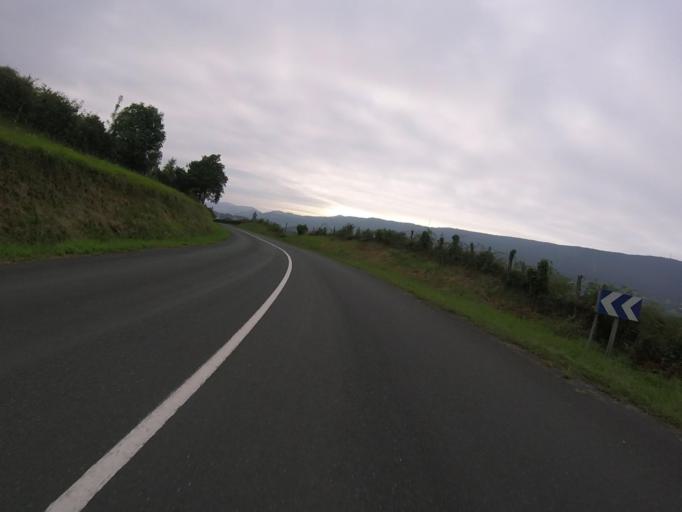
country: ES
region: Basque Country
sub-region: Provincia de Guipuzcoa
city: Lezo
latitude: 43.3147
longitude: -1.8621
